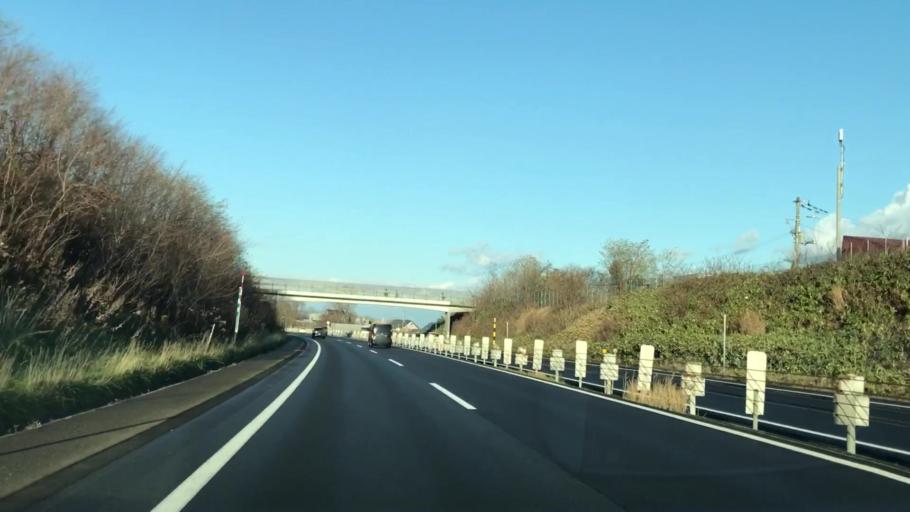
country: JP
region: Hokkaido
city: Sapporo
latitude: 43.1165
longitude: 141.2325
